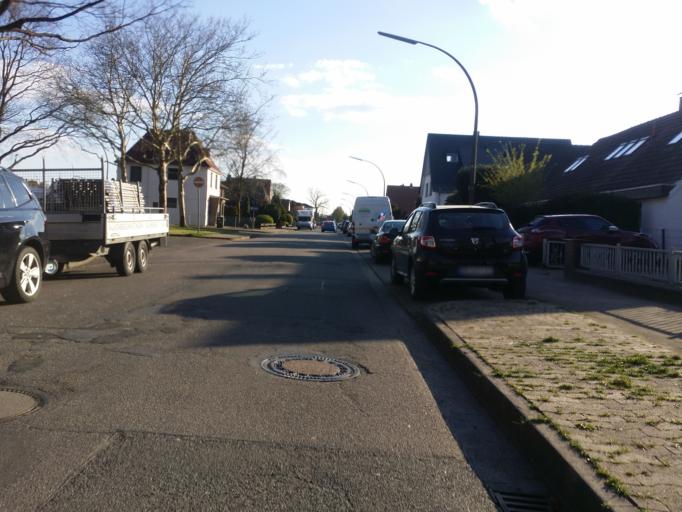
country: DE
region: Lower Saxony
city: Delmenhorst
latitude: 53.0271
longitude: 8.6260
